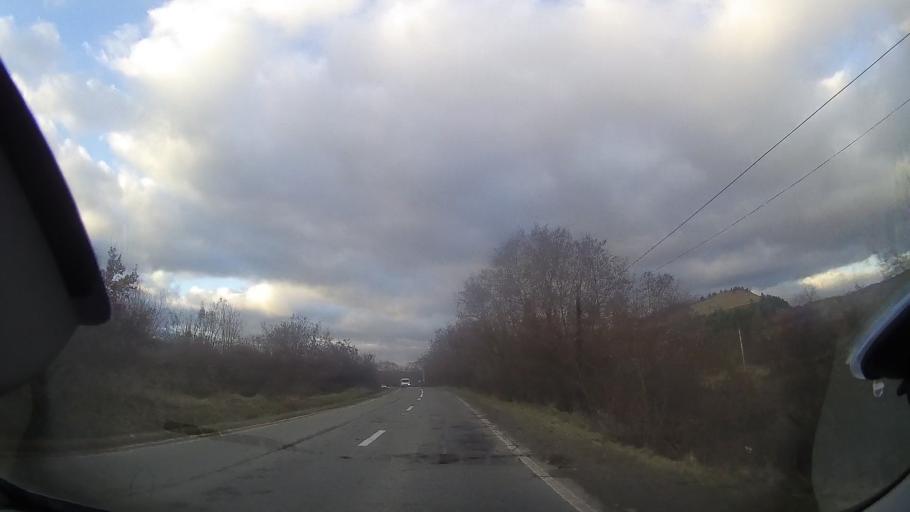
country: RO
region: Cluj
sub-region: Comuna Calatele
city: Calatele
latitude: 46.7837
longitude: 23.0043
